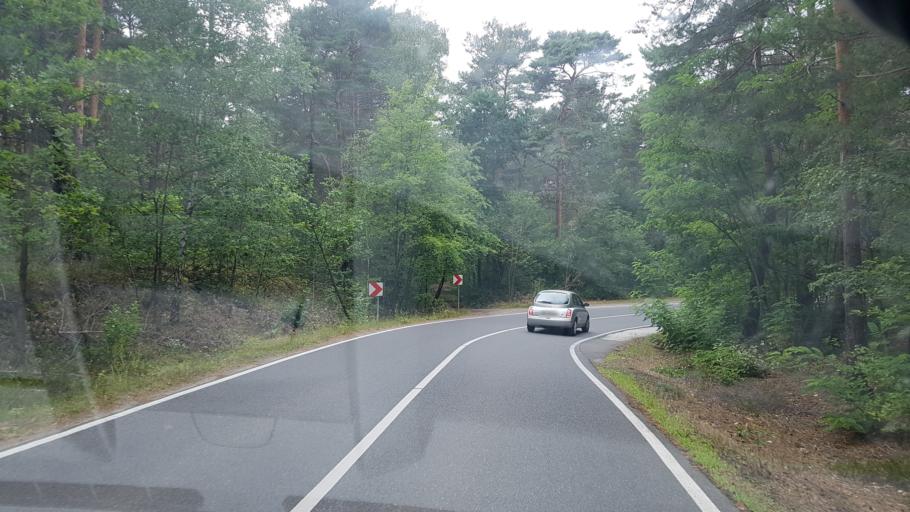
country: DE
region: Brandenburg
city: Spremberg
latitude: 51.5017
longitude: 14.4179
